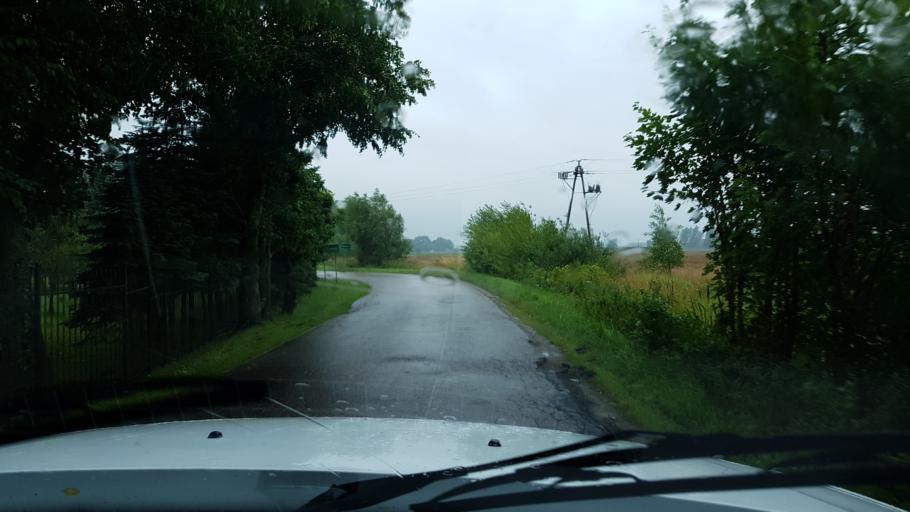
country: PL
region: West Pomeranian Voivodeship
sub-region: Powiat kolobrzeski
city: Ustronie Morskie
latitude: 54.2143
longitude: 15.8599
